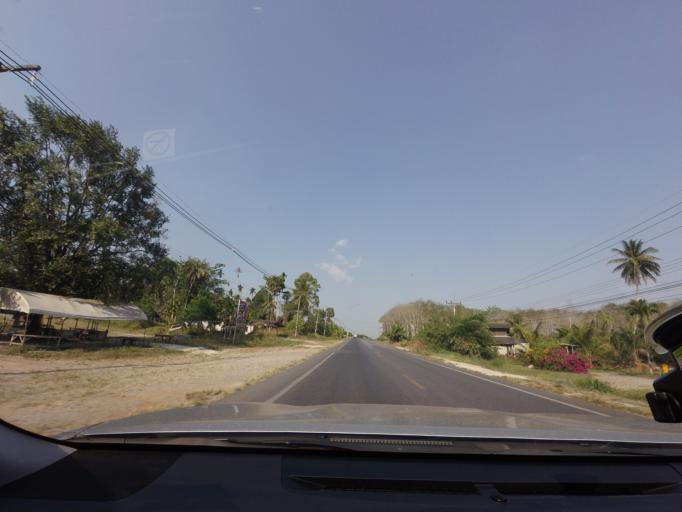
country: TH
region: Surat Thani
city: Phrasaeng
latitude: 8.5605
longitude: 99.1751
